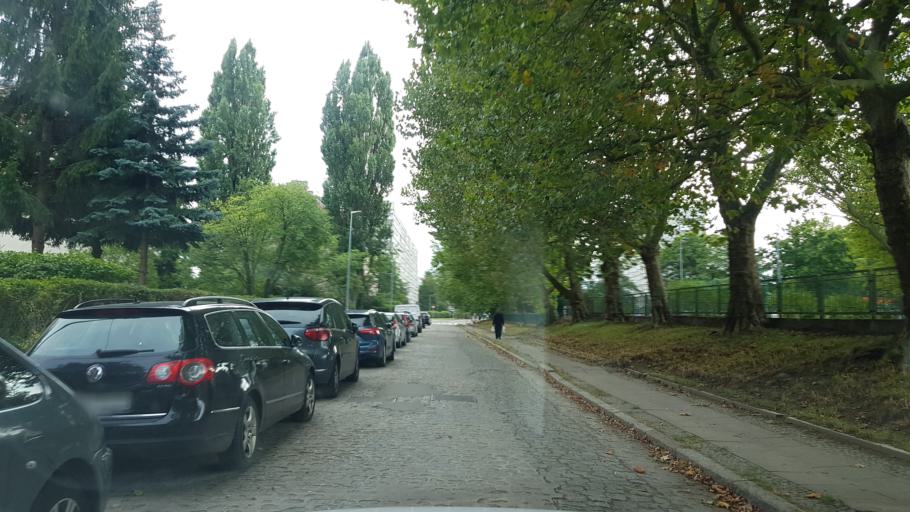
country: PL
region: West Pomeranian Voivodeship
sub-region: Szczecin
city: Szczecin
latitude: 53.4341
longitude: 14.5056
